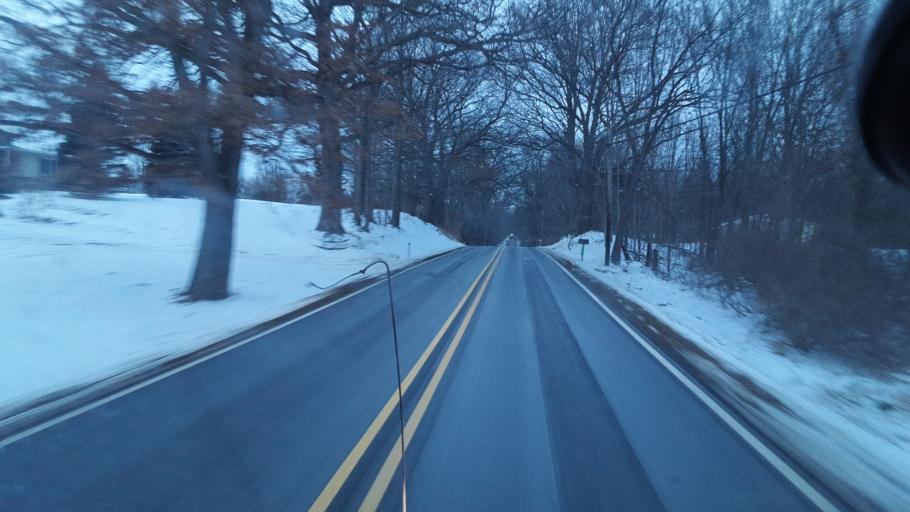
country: US
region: Michigan
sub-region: Jackson County
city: Grass Lake
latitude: 42.3188
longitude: -84.2096
